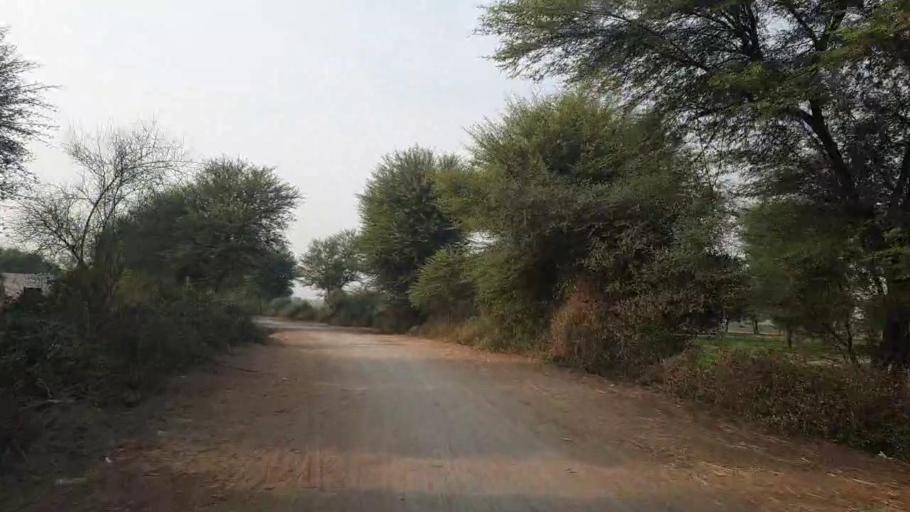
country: PK
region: Sindh
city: Sann
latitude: 26.1421
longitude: 68.0486
